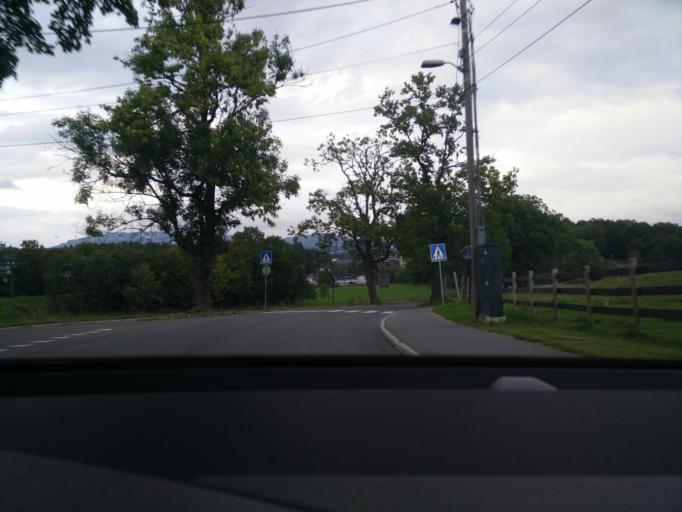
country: NO
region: Oslo
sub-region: Oslo
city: Sjolyststranda
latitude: 59.9121
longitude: 10.6793
